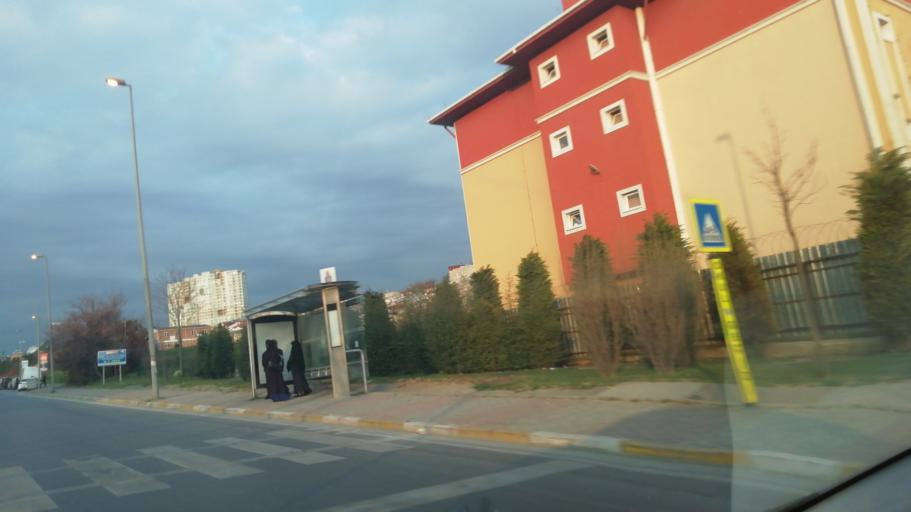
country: TR
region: Istanbul
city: Mahmutbey
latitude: 41.0239
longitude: 28.7837
